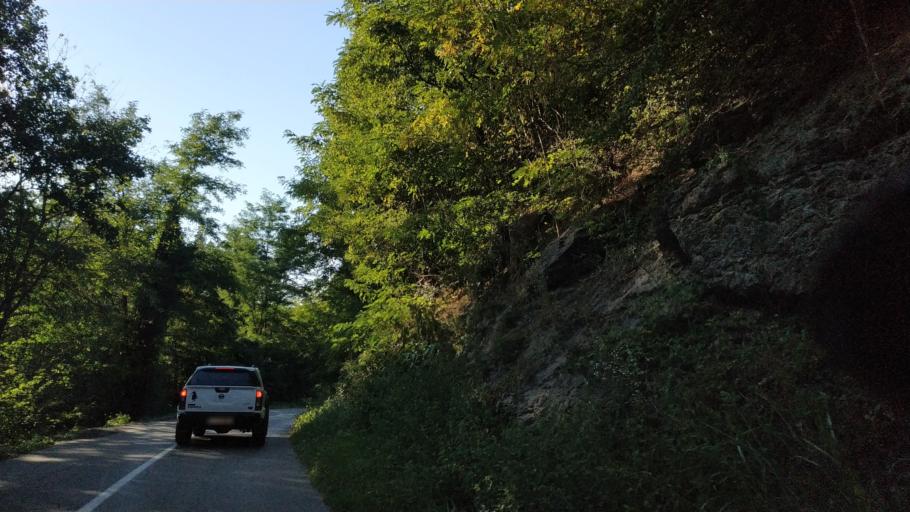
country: RS
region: Central Serbia
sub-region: Rasinski Okrug
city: Krusevac
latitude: 43.4695
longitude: 21.3580
